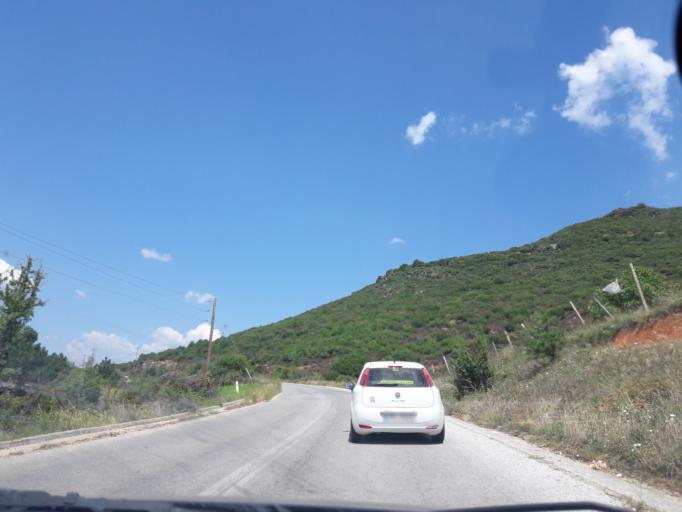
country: GR
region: Central Macedonia
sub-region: Nomos Chalkidikis
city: Polygyros
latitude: 40.3655
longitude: 23.4646
